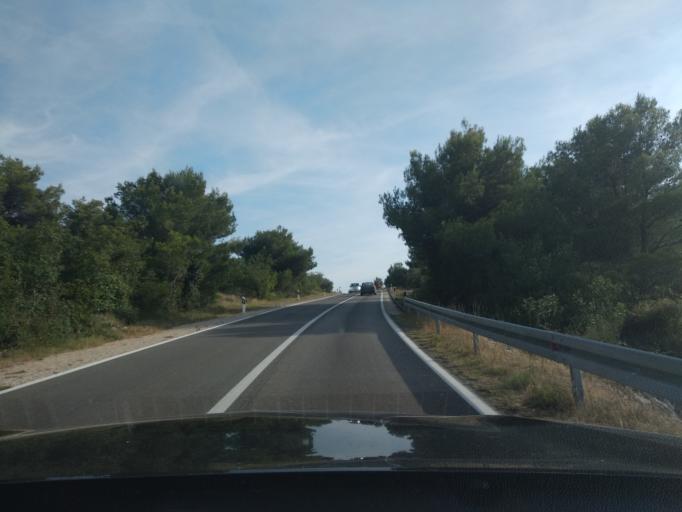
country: HR
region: Sibensko-Kniniska
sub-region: Grad Sibenik
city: Tisno
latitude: 43.7949
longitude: 15.6332
